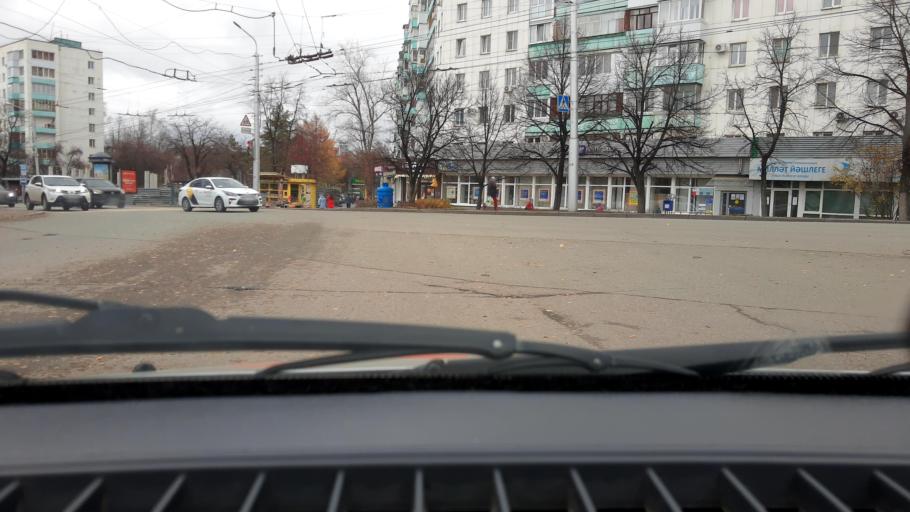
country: RU
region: Bashkortostan
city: Ufa
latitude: 54.7446
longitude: 56.0267
